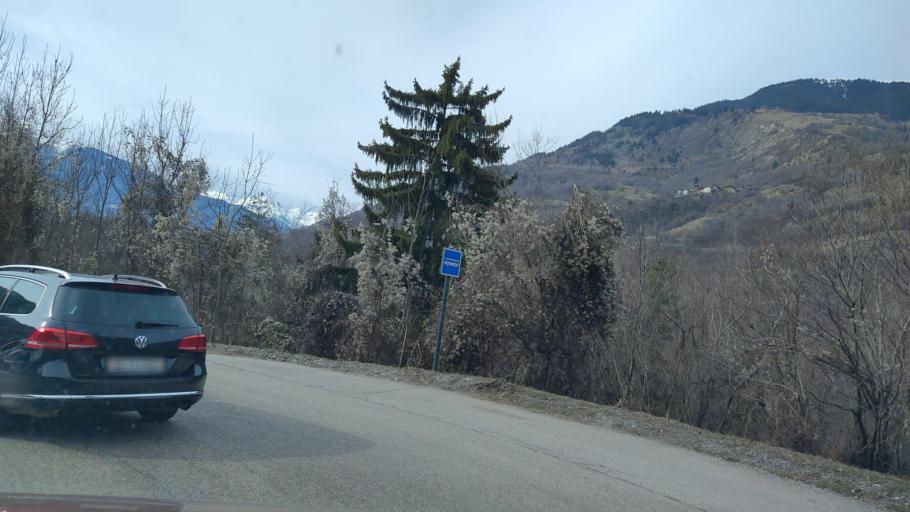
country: FR
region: Rhone-Alpes
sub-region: Departement de la Savoie
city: Saint-Bon-Tarentaise
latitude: 45.4424
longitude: 6.6188
